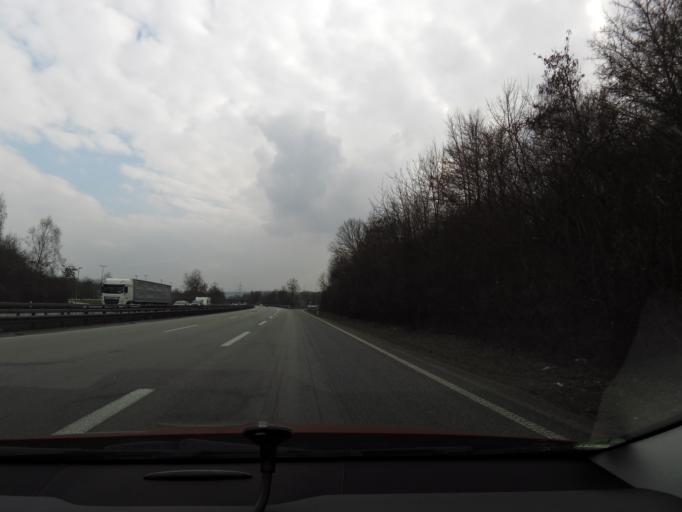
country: DE
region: Rheinland-Pfalz
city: Armsheim
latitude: 49.8070
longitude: 8.0509
